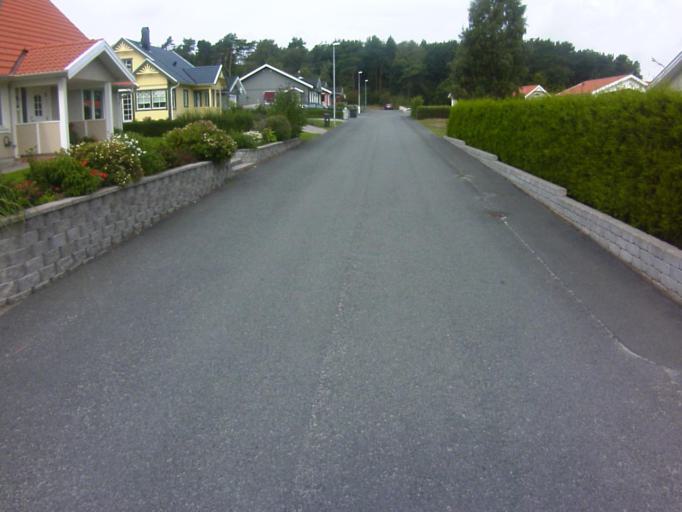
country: SE
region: Blekinge
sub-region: Karlshamns Kommun
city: Morrum
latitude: 56.0453
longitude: 14.7569
